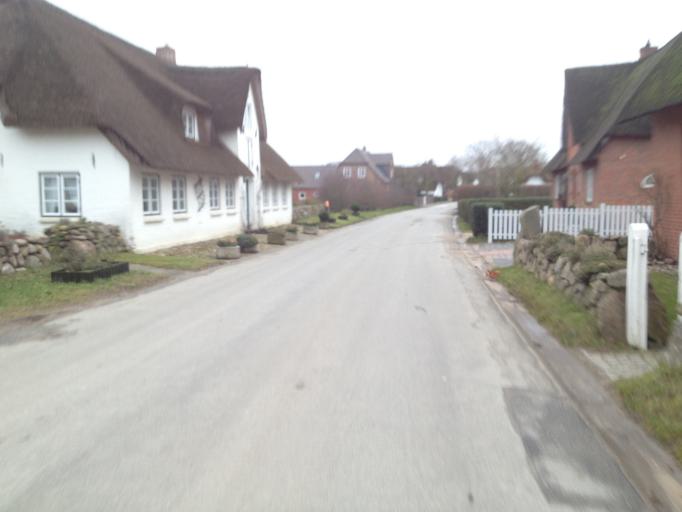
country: DE
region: Schleswig-Holstein
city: Nebel
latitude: 54.6552
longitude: 8.3528
